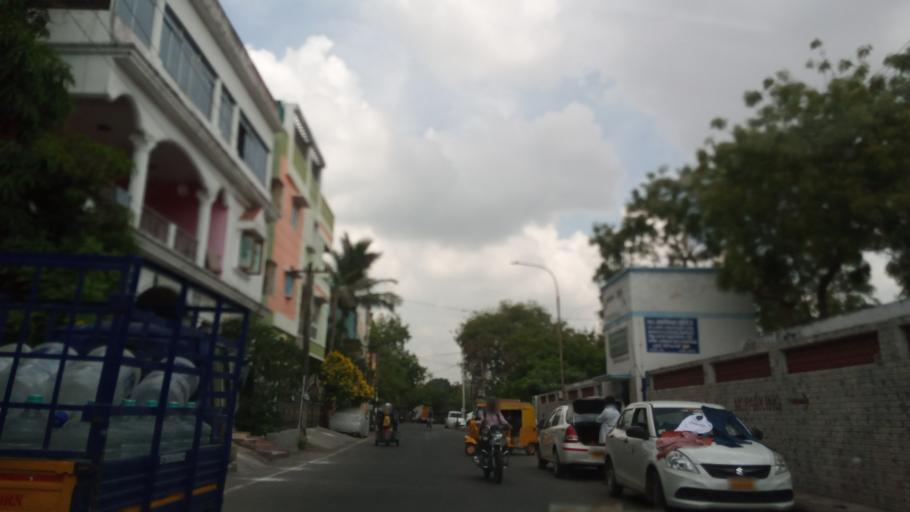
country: IN
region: Tamil Nadu
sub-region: Kancheepuram
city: Madipakkam
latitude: 12.9816
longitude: 80.1790
